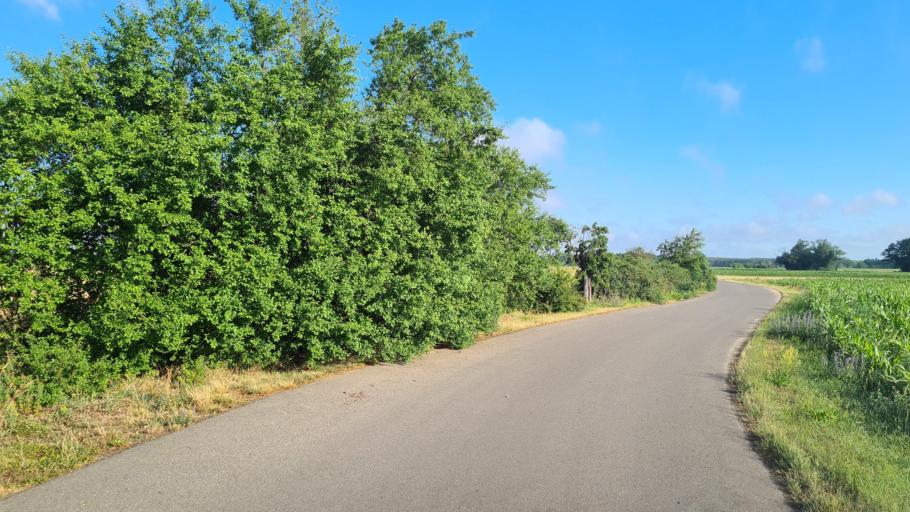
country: DE
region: Brandenburg
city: Falkenberg
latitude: 51.5857
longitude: 13.2087
